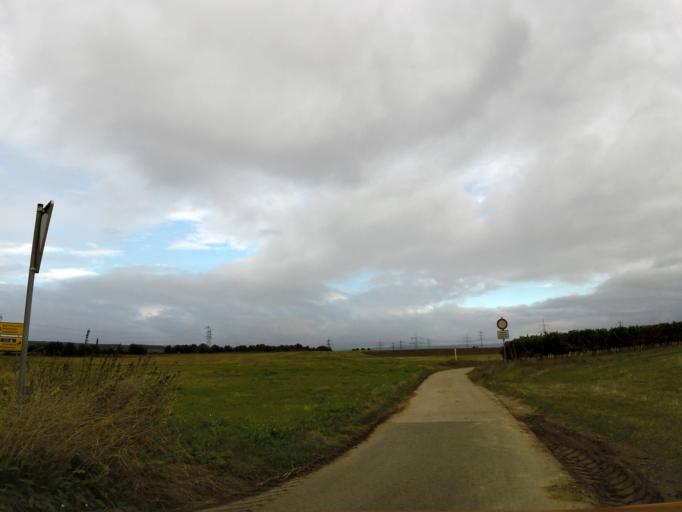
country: DE
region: Rheinland-Pfalz
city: Roxheim
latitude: 49.8829
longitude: 7.8222
